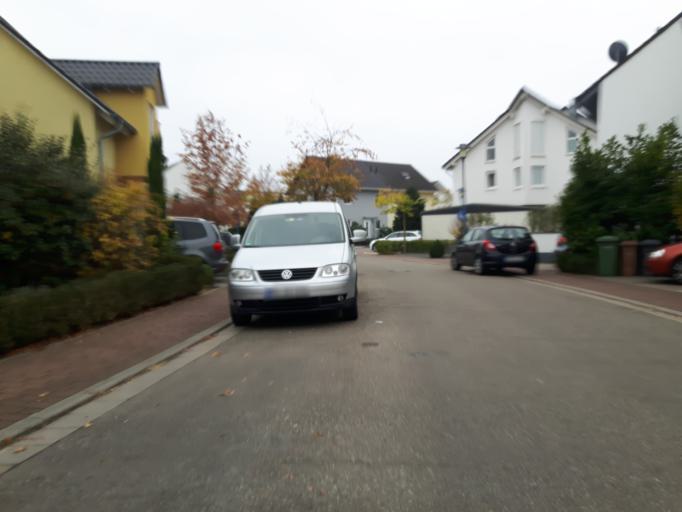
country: DE
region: Baden-Wuerttemberg
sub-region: Karlsruhe Region
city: Hockenheim
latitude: 49.3085
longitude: 8.5452
